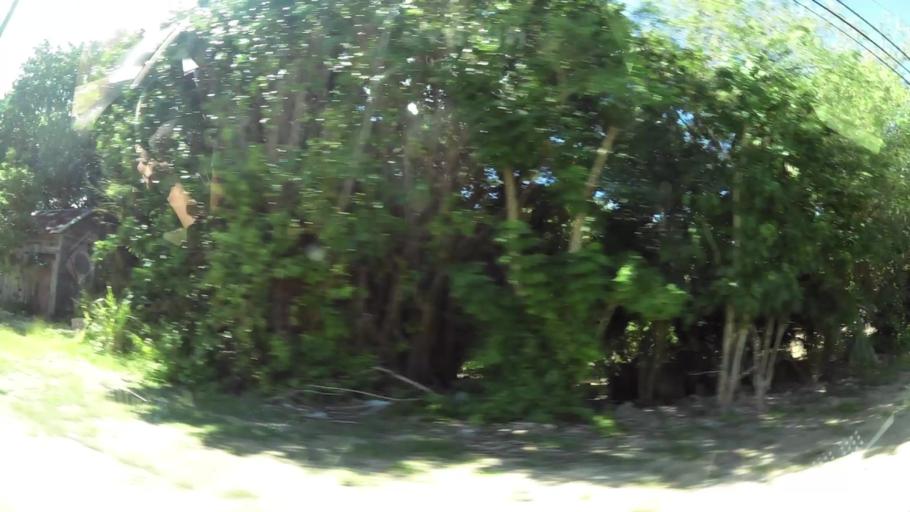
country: GP
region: Guadeloupe
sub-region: Guadeloupe
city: Petit-Canal
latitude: 16.3938
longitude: -61.4617
